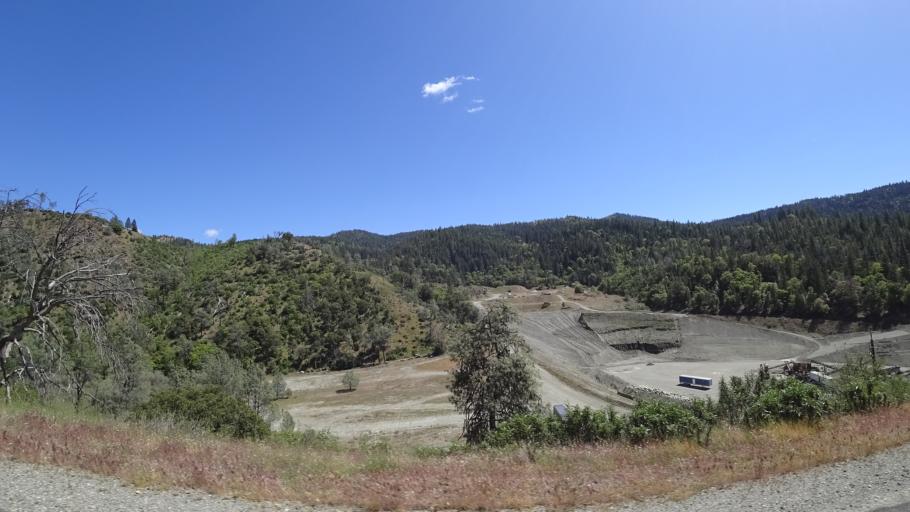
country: US
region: California
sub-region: Trinity County
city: Weaverville
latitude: 40.7357
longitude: -123.0097
